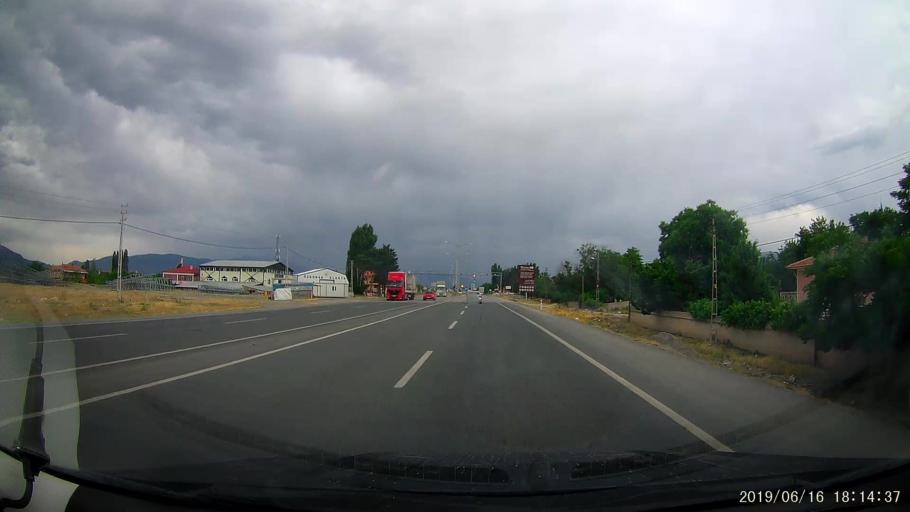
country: TR
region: Erzincan
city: Erzincan
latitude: 39.7253
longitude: 39.5555
